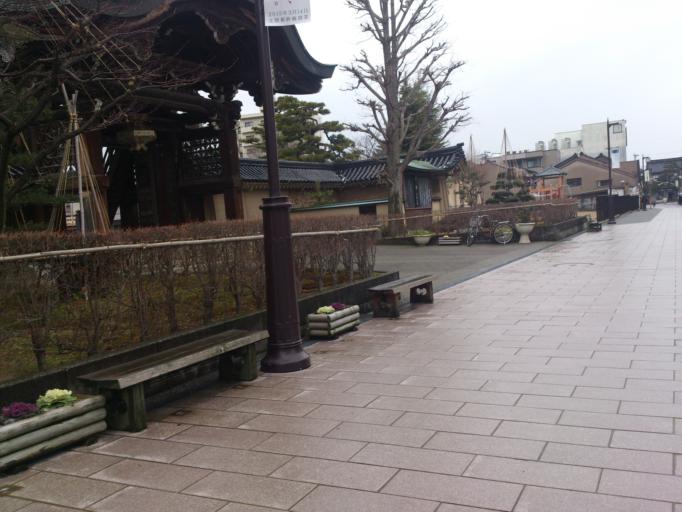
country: JP
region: Ishikawa
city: Kanazawa-shi
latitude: 36.5747
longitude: 136.6556
